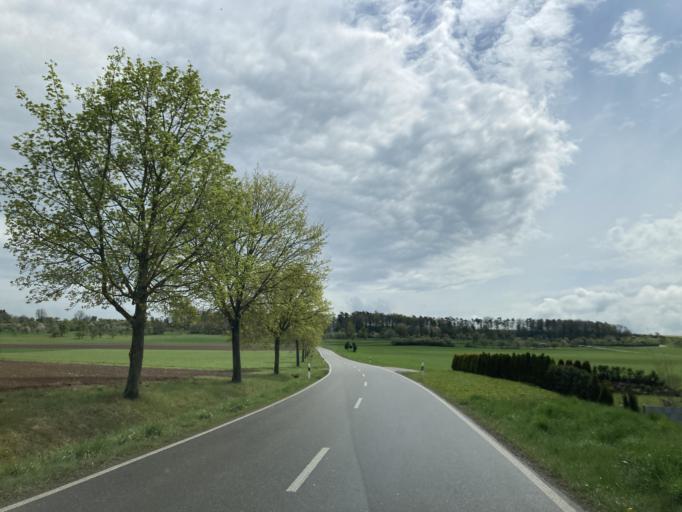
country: DE
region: Baden-Wuerttemberg
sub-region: Regierungsbezirk Stuttgart
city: Bondorf
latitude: 48.5247
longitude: 8.8677
